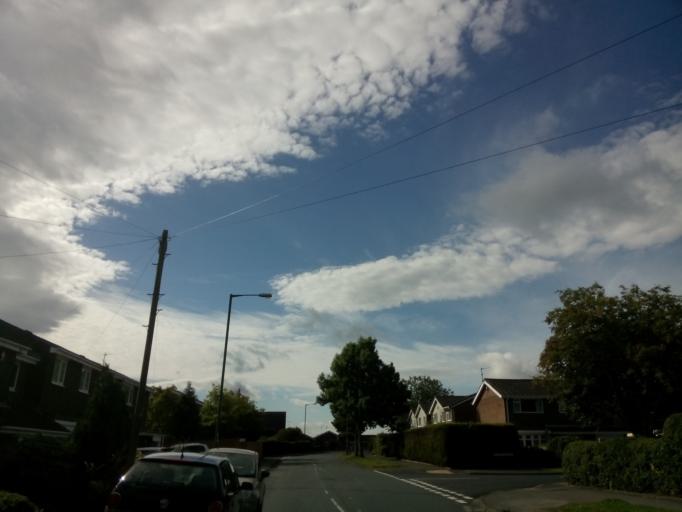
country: GB
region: England
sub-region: County Durham
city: Durham
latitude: 54.8008
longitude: -1.5633
